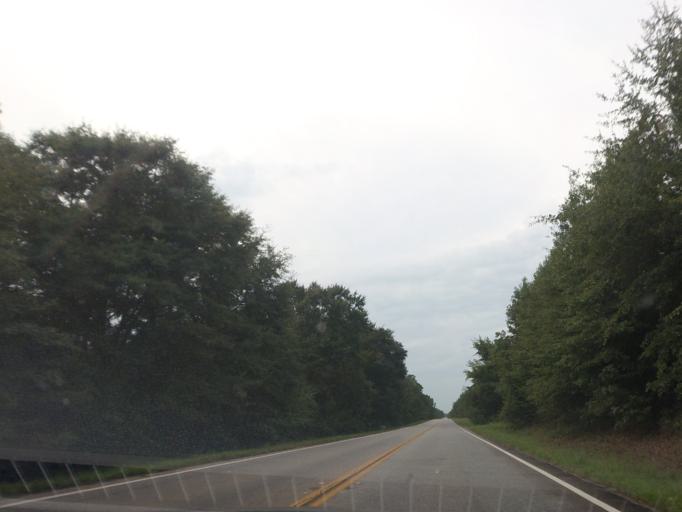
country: US
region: Georgia
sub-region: Twiggs County
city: Jeffersonville
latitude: 32.6934
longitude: -83.3733
